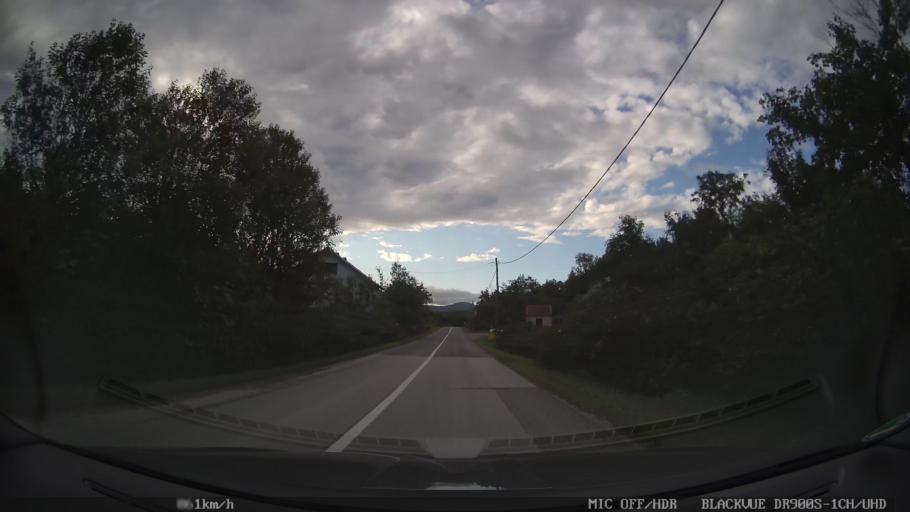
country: HR
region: Karlovacka
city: Plaski
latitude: 44.9937
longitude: 15.4468
